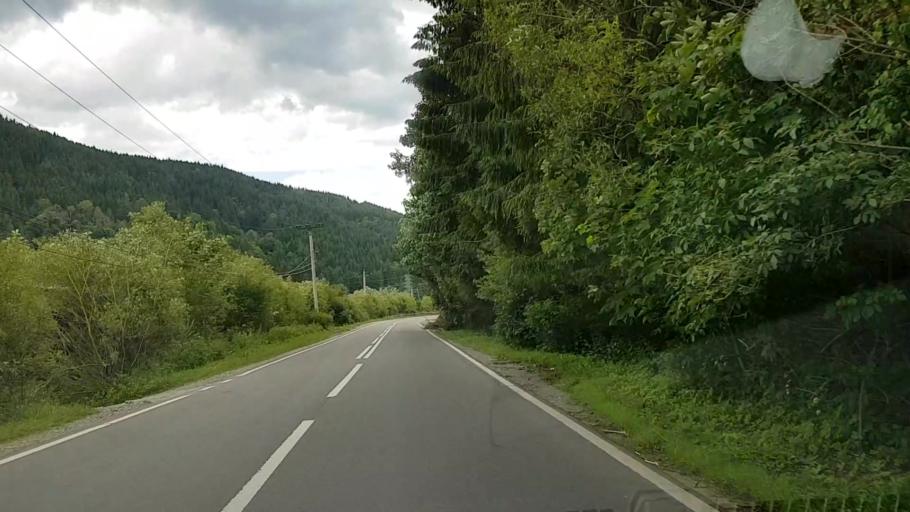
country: RO
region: Neamt
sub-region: Comuna Poiana Teiului
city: Poiana Teiului
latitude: 47.1044
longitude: 25.9374
